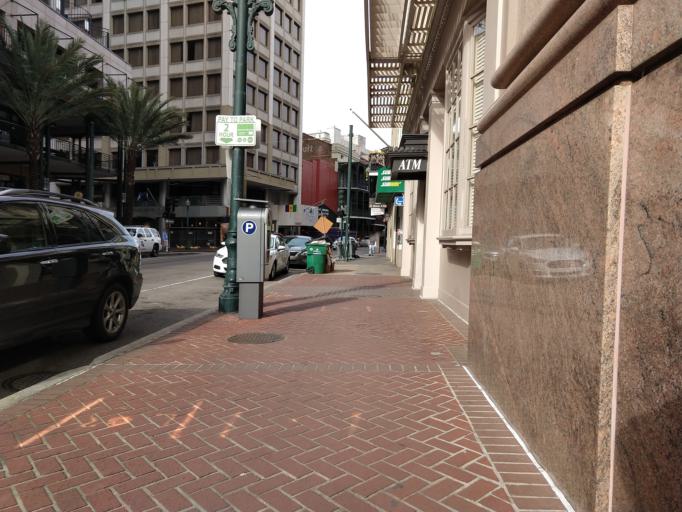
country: US
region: Louisiana
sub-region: Orleans Parish
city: New Orleans
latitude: 29.9520
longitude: -90.0702
